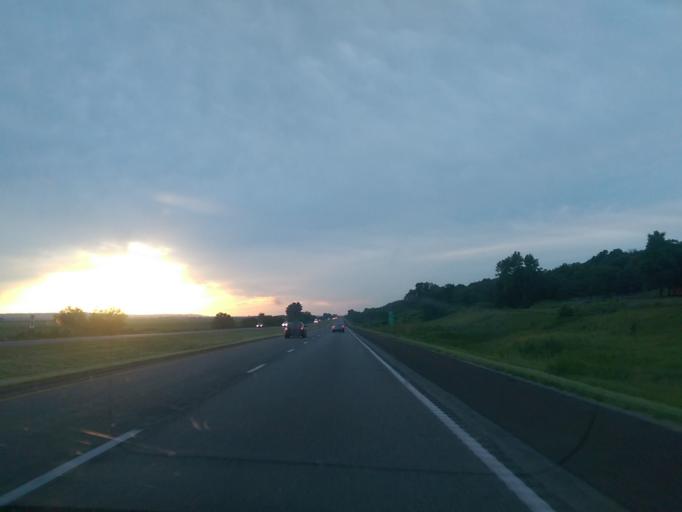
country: US
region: Missouri
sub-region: Holt County
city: Mound City
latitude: 40.2147
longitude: -95.3825
